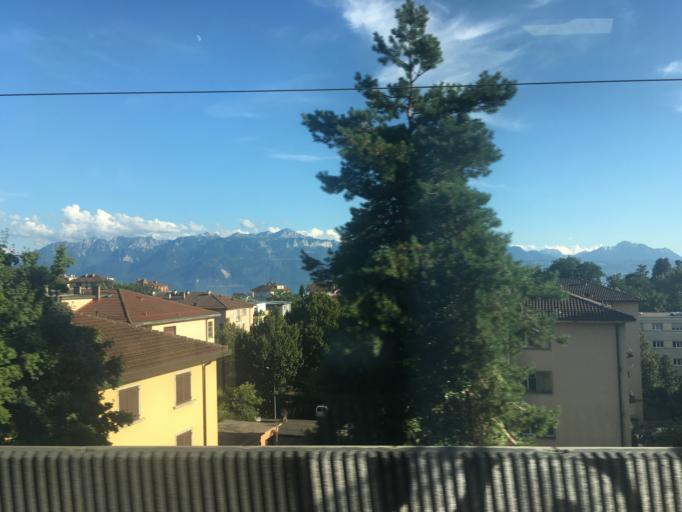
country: CH
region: Vaud
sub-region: Lausanne District
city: Lausanne
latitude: 46.5144
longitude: 6.6451
